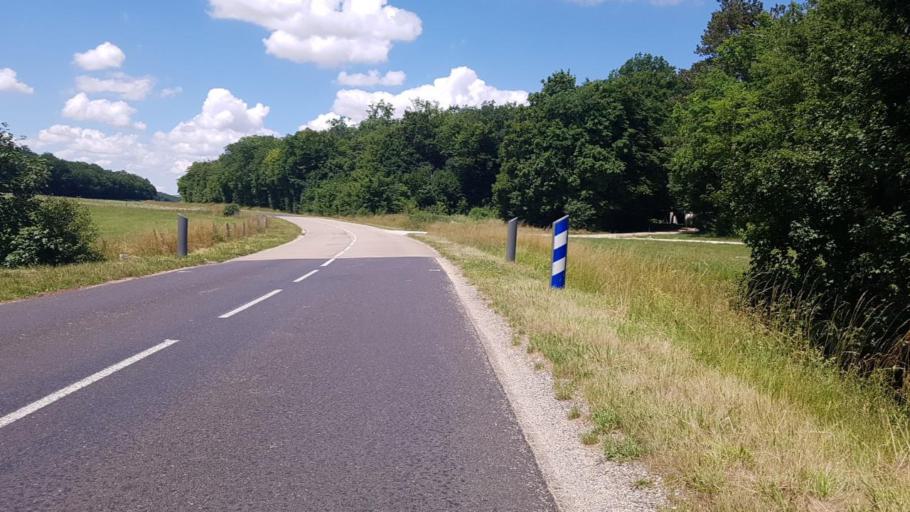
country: FR
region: Lorraine
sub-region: Departement de la Meuse
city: Vacon
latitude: 48.6731
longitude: 5.5906
